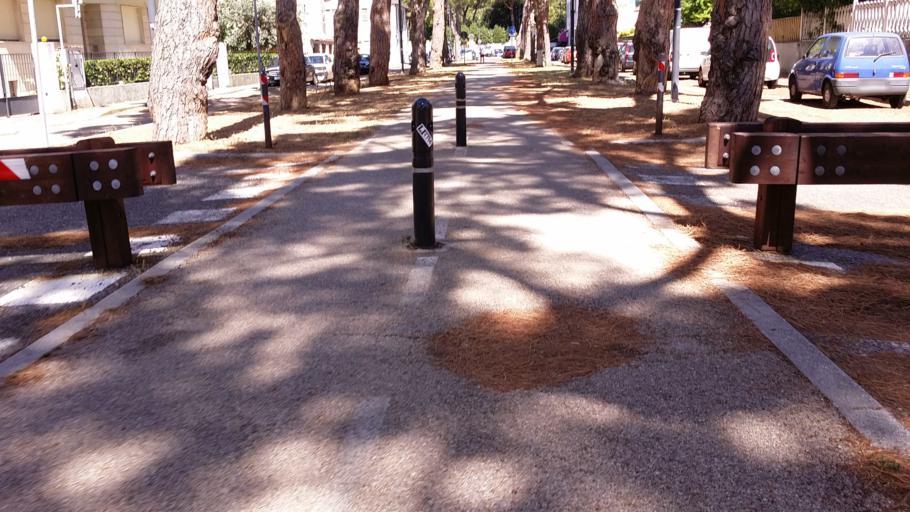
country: IT
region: Tuscany
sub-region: Provincia di Livorno
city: Livorno
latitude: 43.5349
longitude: 10.3191
